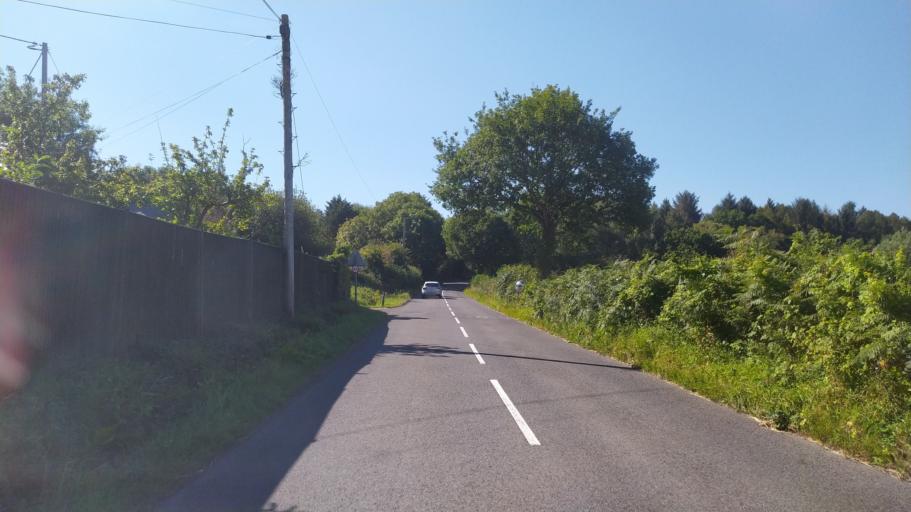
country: GB
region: England
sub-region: Dorset
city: Lytchett Matravers
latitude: 50.7506
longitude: -2.1234
